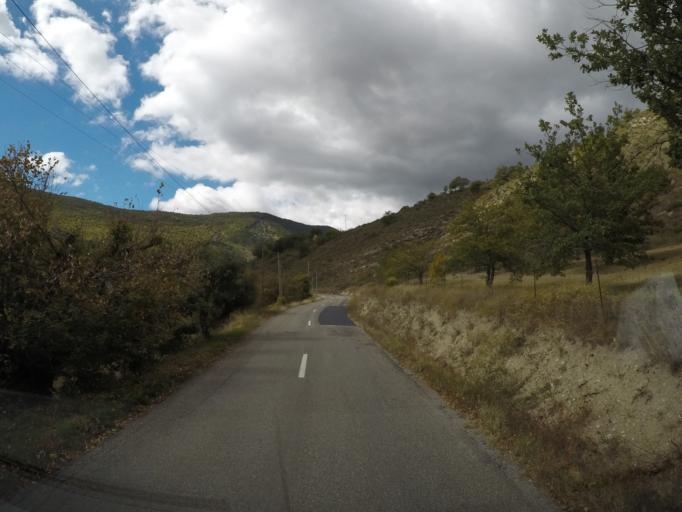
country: FR
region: Provence-Alpes-Cote d'Azur
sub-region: Departement du Vaucluse
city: Sault
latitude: 44.1732
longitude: 5.5998
